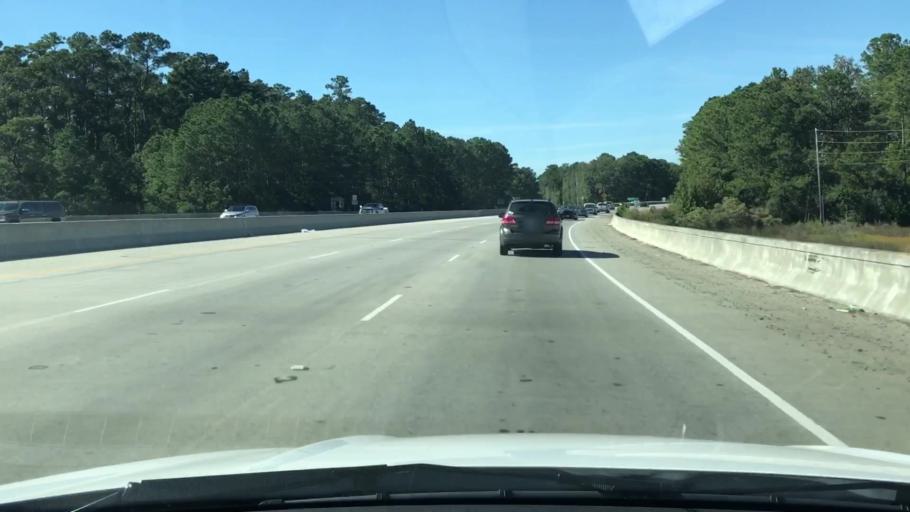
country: US
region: South Carolina
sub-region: Beaufort County
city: Bluffton
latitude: 32.2894
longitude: -80.9296
